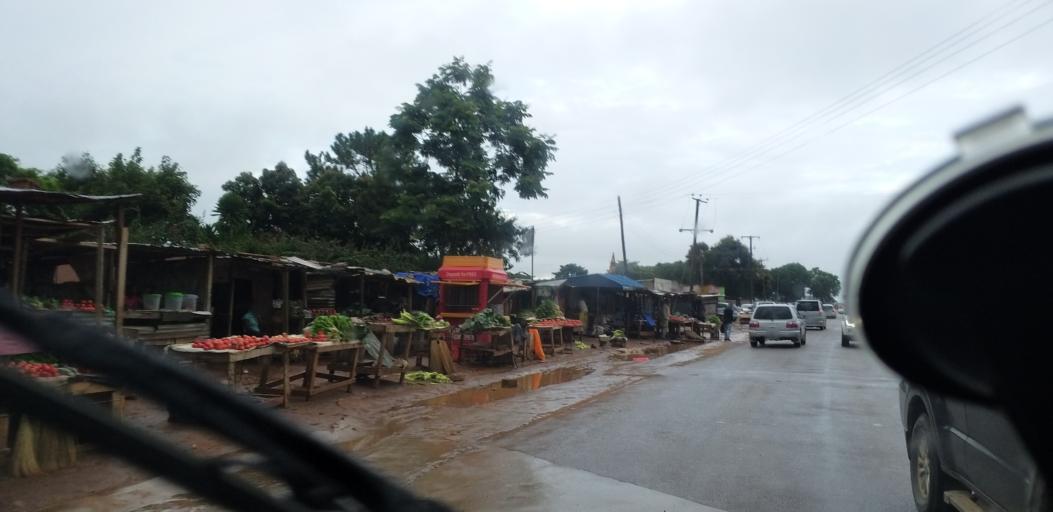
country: ZM
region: Lusaka
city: Lusaka
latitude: -15.5130
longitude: 28.2991
